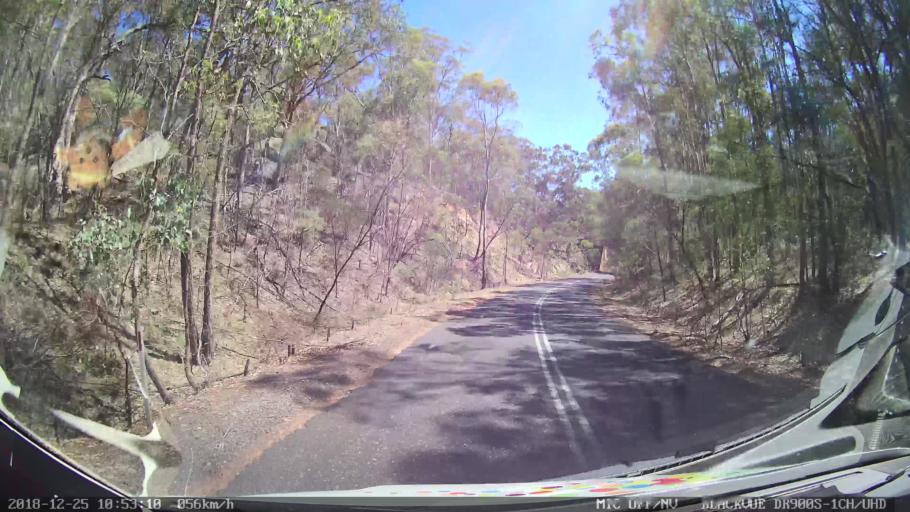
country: AU
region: New South Wales
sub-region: Upper Hunter Shire
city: Merriwa
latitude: -32.4223
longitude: 150.2728
